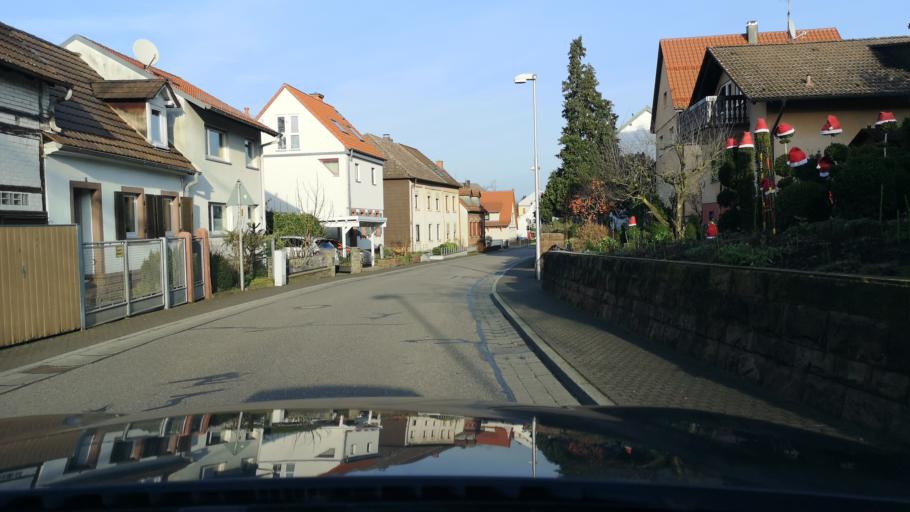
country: DE
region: Baden-Wuerttemberg
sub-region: Karlsruhe Region
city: Ettlingen
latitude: 48.9733
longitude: 8.4520
